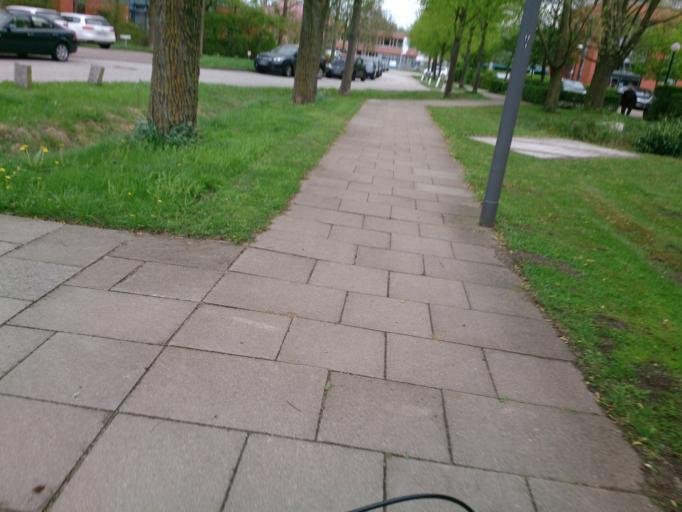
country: DE
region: Hamburg
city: Harburg
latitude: 53.4734
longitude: 9.9324
